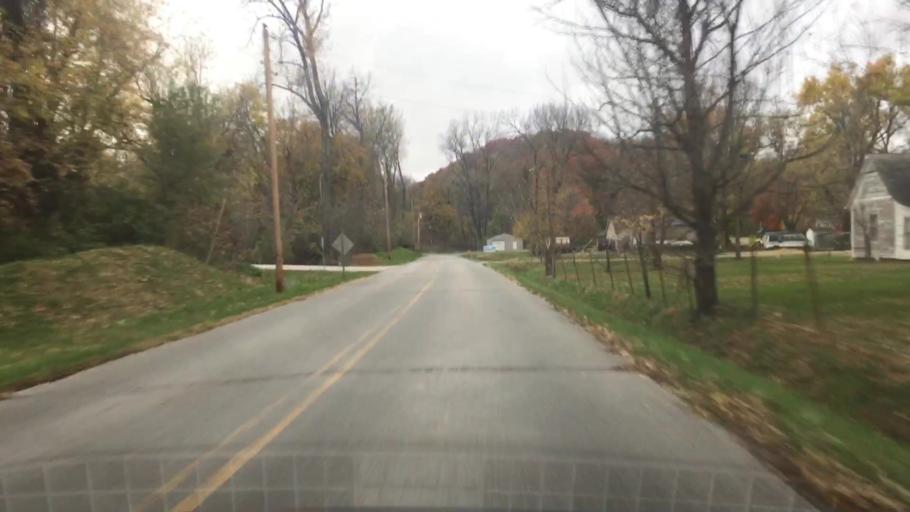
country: US
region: Missouri
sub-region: Boone County
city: Columbia
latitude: 38.9098
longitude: -92.4720
